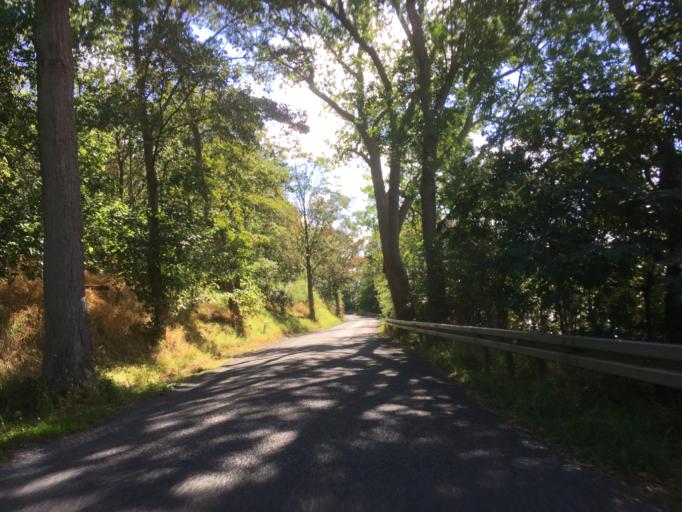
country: DE
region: Brandenburg
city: Angermunde
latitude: 52.9605
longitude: 14.0031
